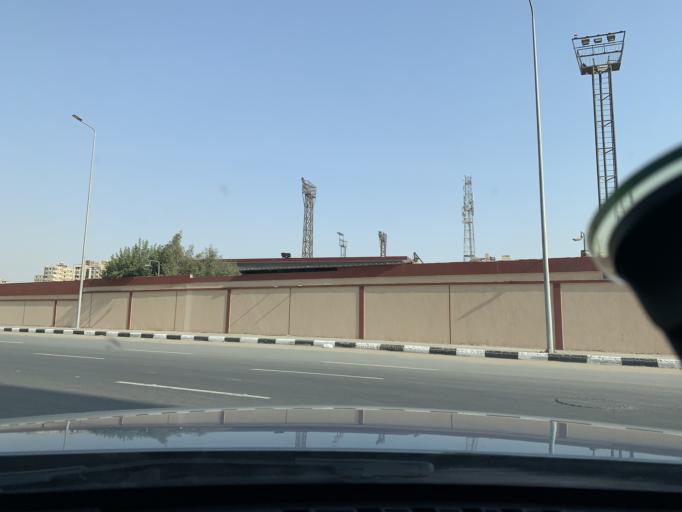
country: EG
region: Muhafazat al Qalyubiyah
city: Al Khankah
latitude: 30.1286
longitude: 31.3639
